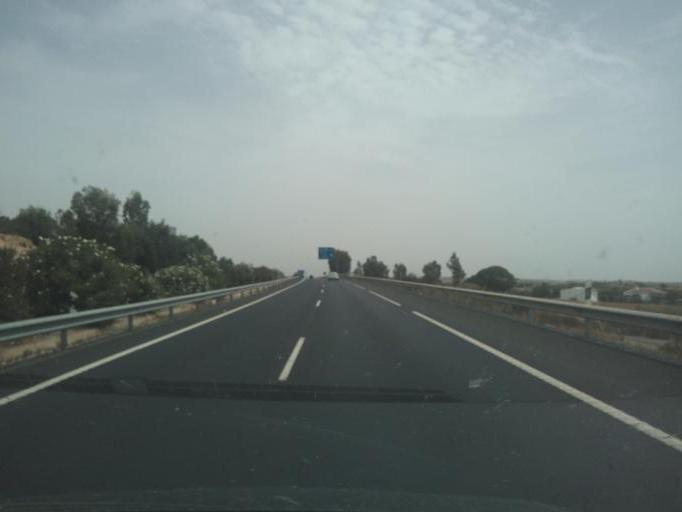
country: ES
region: Andalusia
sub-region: Provincia de Huelva
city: Bollullos par del Condado
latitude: 37.3525
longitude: -6.5745
